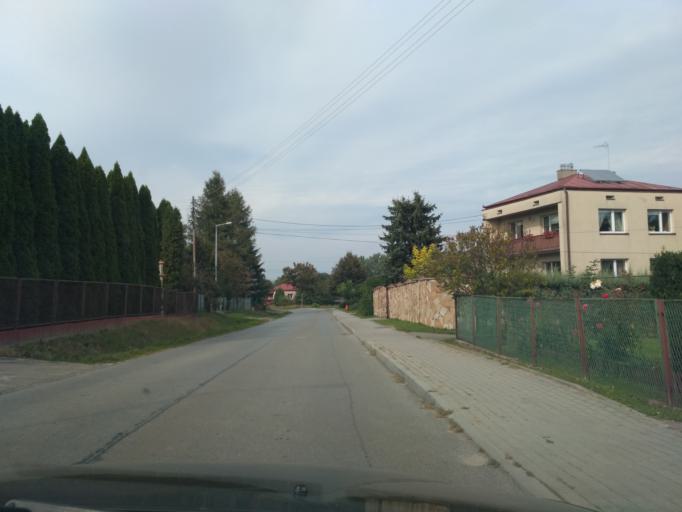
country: PL
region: Subcarpathian Voivodeship
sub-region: Powiat rzeszowski
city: Trzciana
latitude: 50.0628
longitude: 21.8350
